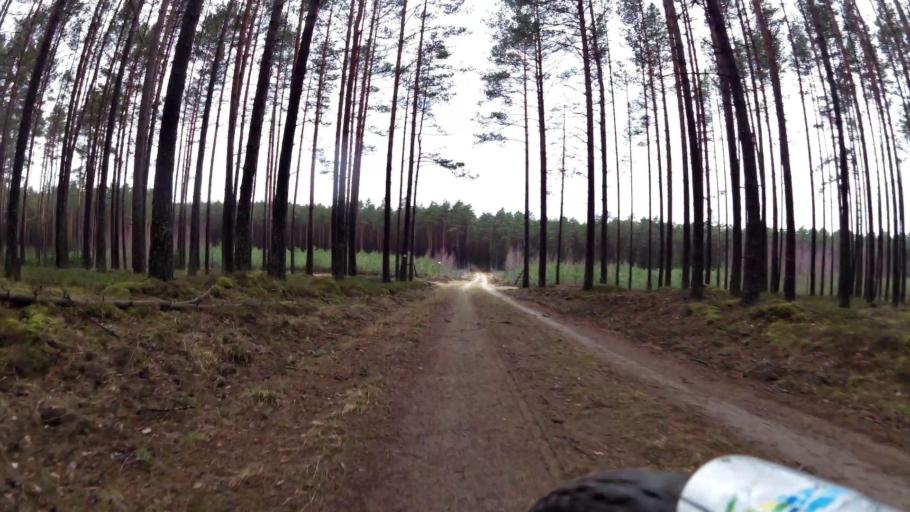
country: PL
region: Pomeranian Voivodeship
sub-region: Powiat bytowski
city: Borzytuchom
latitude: 54.2666
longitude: 17.4019
